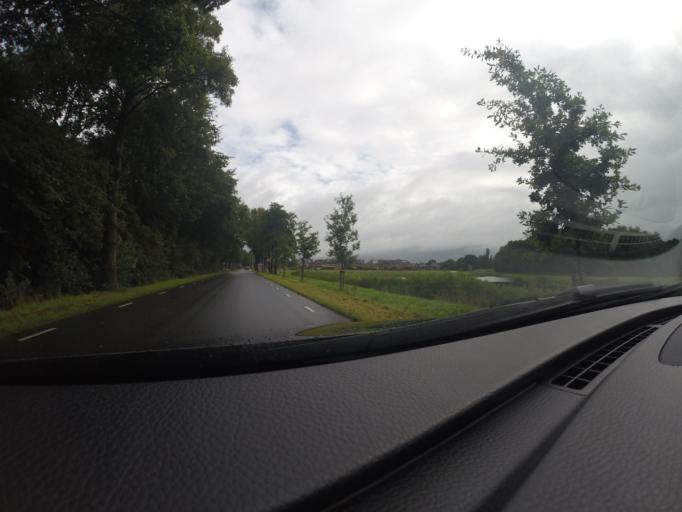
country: NL
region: Gelderland
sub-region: Gemeente Lochem
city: Laren
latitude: 52.2719
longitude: 6.4053
